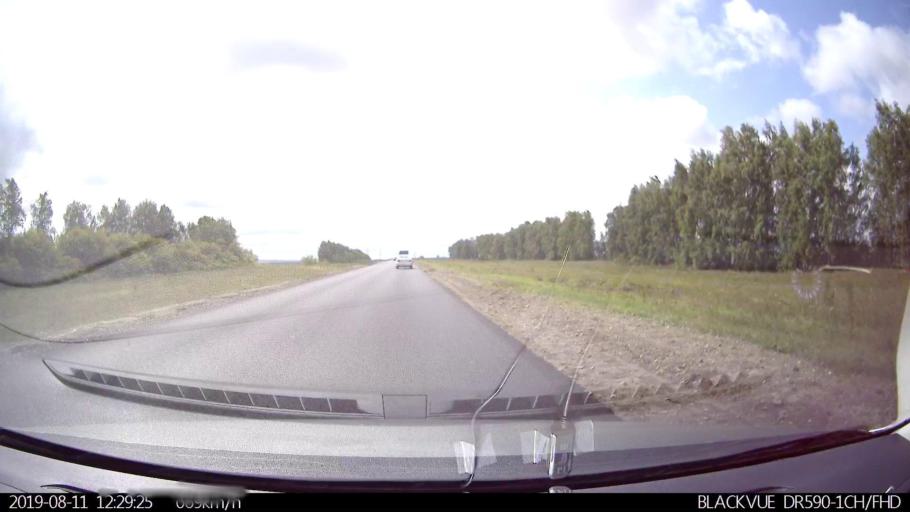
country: RU
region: Ulyanovsk
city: Ignatovka
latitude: 53.8349
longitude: 47.9028
